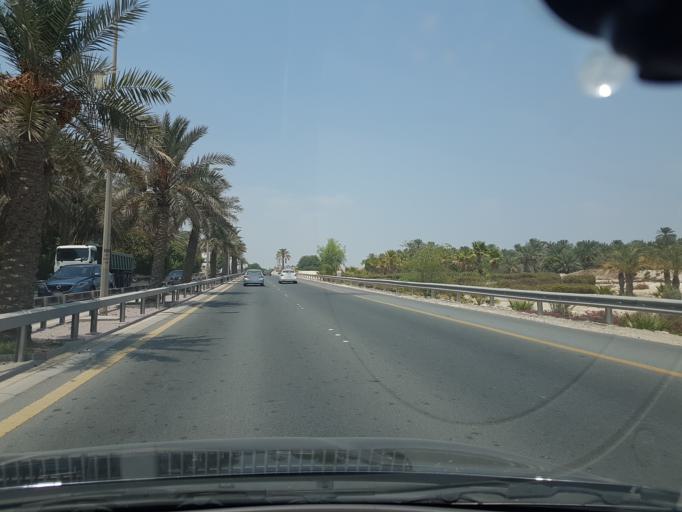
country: BH
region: Northern
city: Ar Rifa'
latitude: 26.1162
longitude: 50.5372
